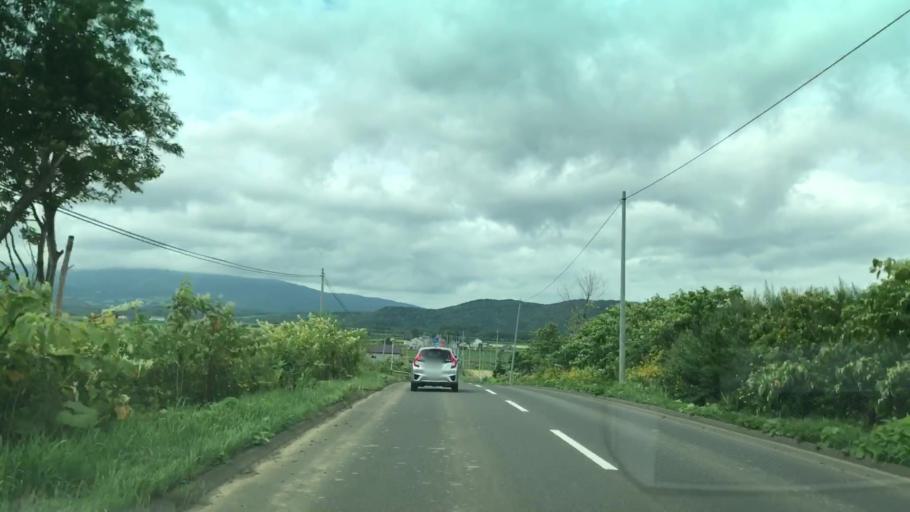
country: JP
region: Hokkaido
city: Niseko Town
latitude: 42.9326
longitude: 140.7865
